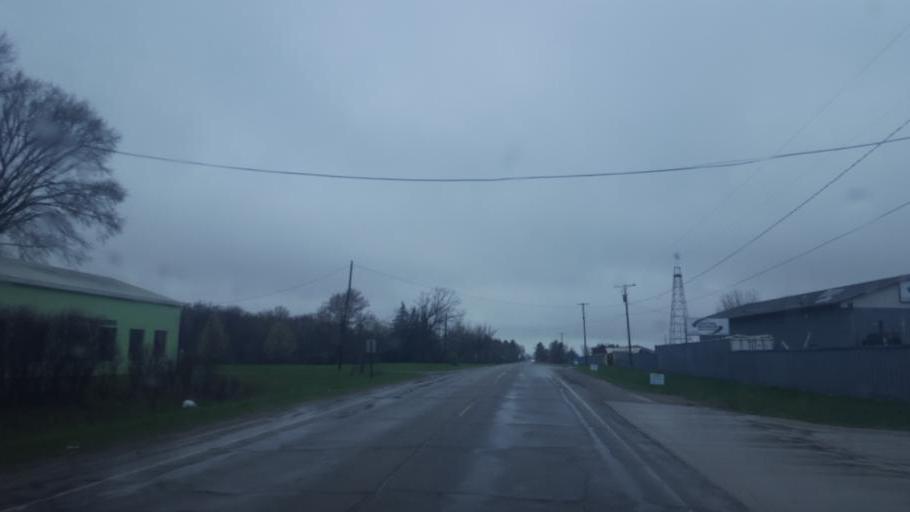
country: US
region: Michigan
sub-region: Isabella County
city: Mount Pleasant
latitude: 43.6318
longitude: -84.7680
